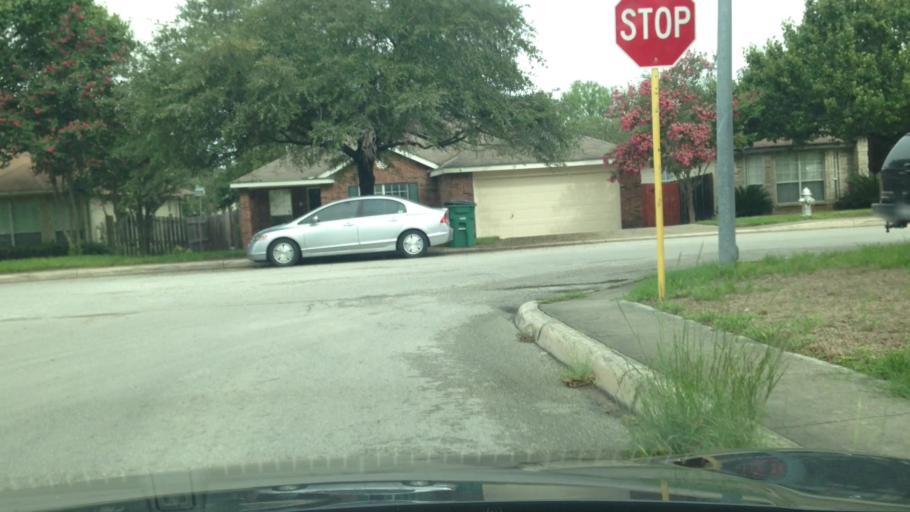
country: US
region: Texas
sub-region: Bexar County
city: Live Oak
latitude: 29.5858
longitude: -98.3880
